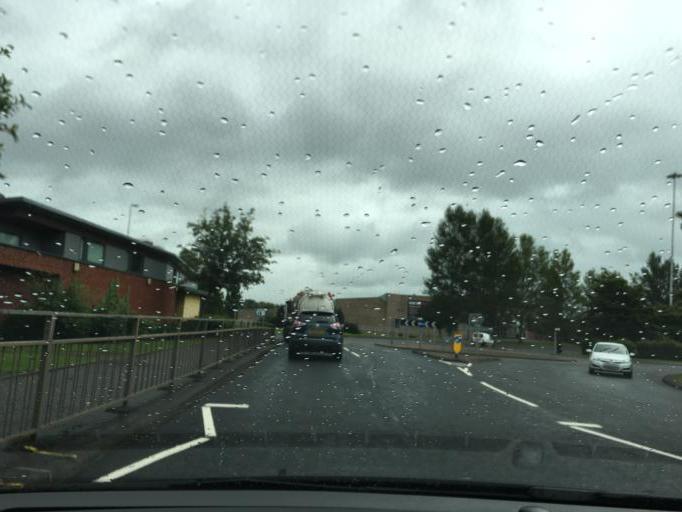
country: GB
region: Scotland
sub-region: North Lanarkshire
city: Motherwell
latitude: 55.7925
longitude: -3.9930
